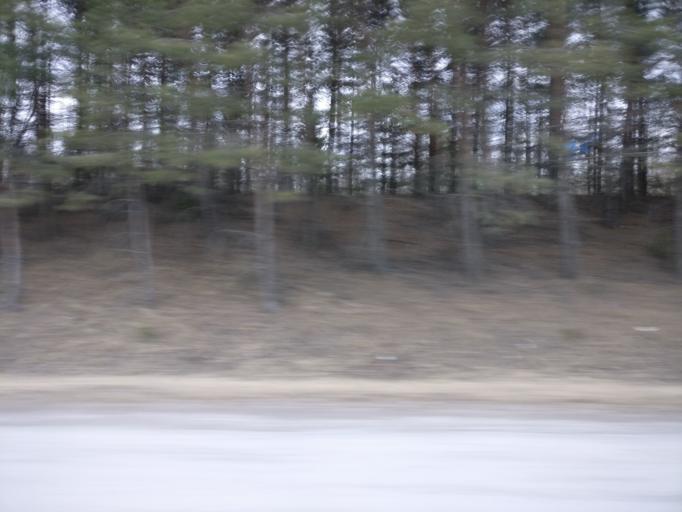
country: FI
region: Uusimaa
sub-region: Helsinki
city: Nurmijaervi
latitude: 60.4861
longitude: 24.8500
